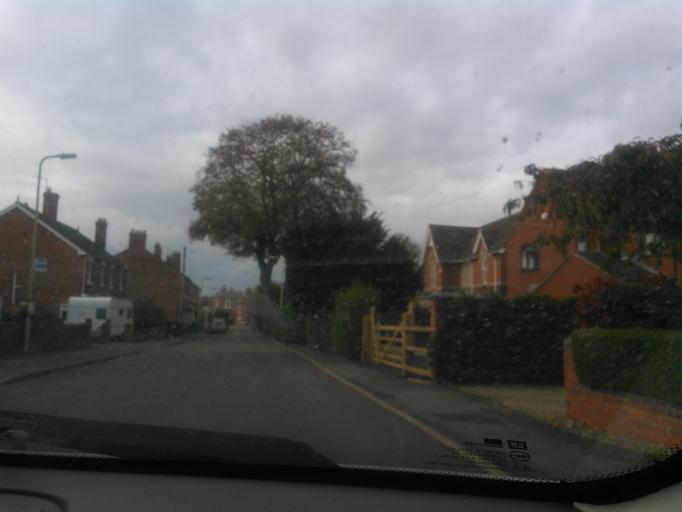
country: GB
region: England
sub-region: Shropshire
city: Wem
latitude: 52.8601
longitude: -2.7203
